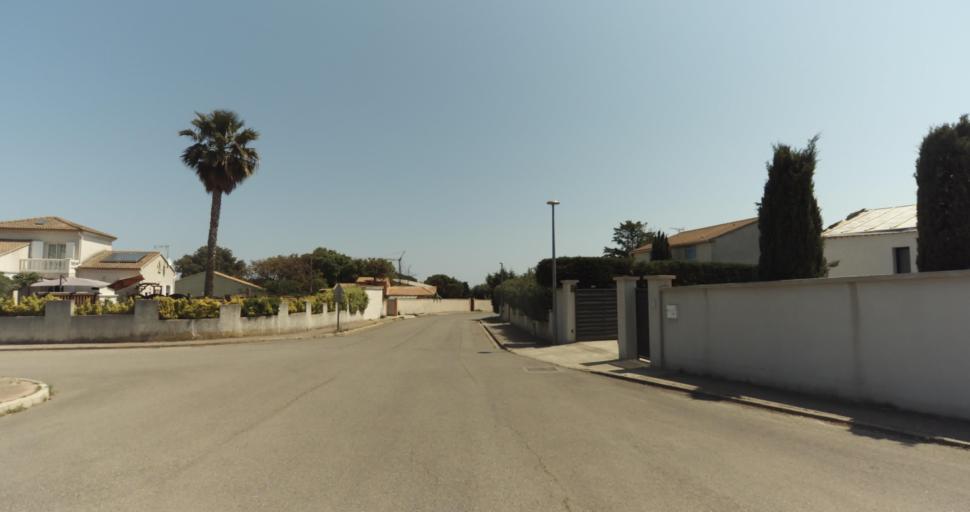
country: FR
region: Corsica
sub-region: Departement de la Haute-Corse
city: Biguglia
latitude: 42.5942
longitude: 9.4327
